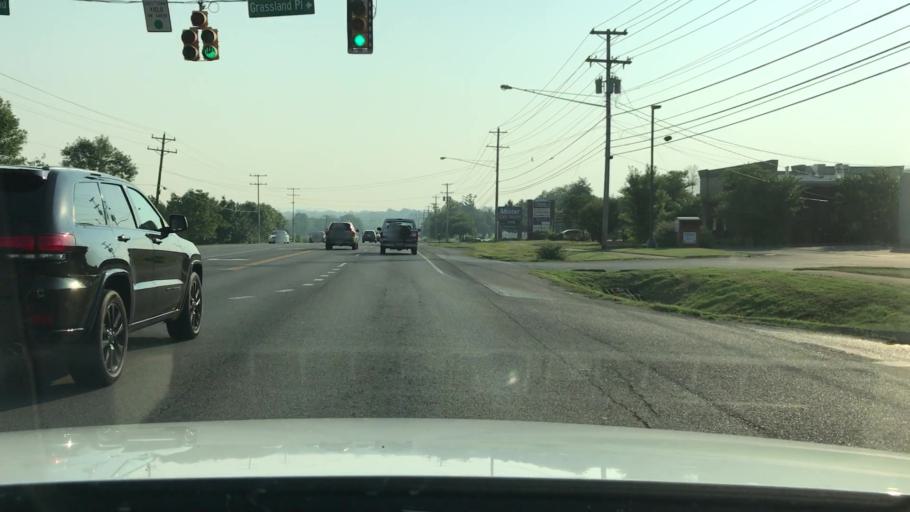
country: US
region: Tennessee
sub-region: Sumner County
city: Gallatin
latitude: 36.3631
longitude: -86.4940
